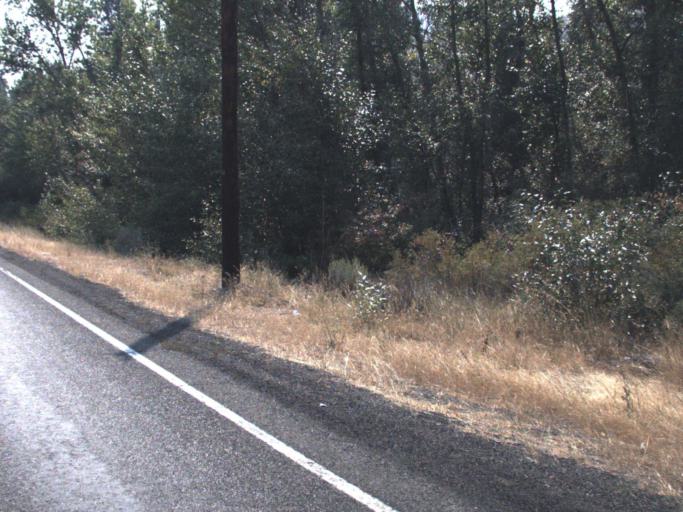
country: US
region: Washington
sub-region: Kittitas County
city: Ellensburg
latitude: 46.9238
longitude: -120.5095
